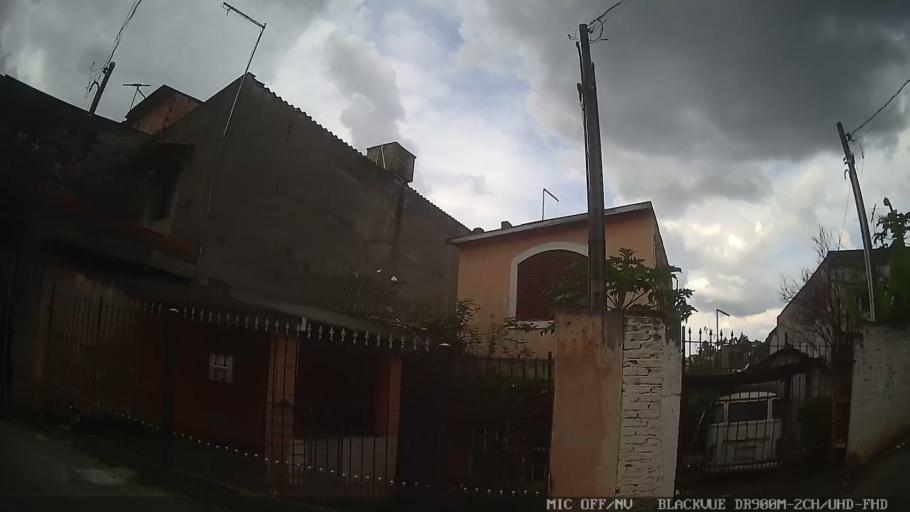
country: BR
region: Sao Paulo
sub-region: Ferraz De Vasconcelos
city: Ferraz de Vasconcelos
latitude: -23.5493
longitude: -46.3643
